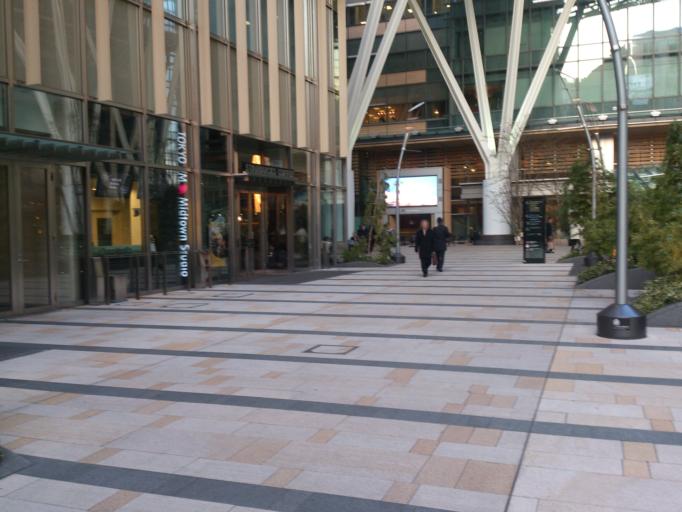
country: JP
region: Tokyo
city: Tokyo
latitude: 35.6652
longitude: 139.7307
